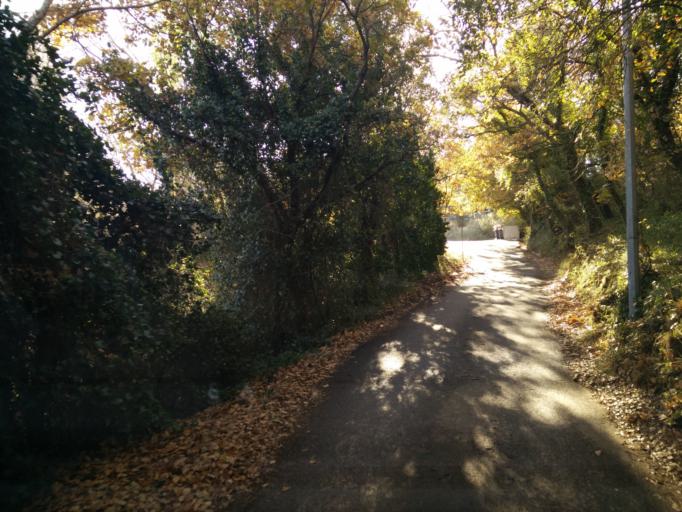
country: FR
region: Provence-Alpes-Cote d'Azur
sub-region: Departement du Var
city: La Garde-Freinet
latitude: 43.3006
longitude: 6.4907
